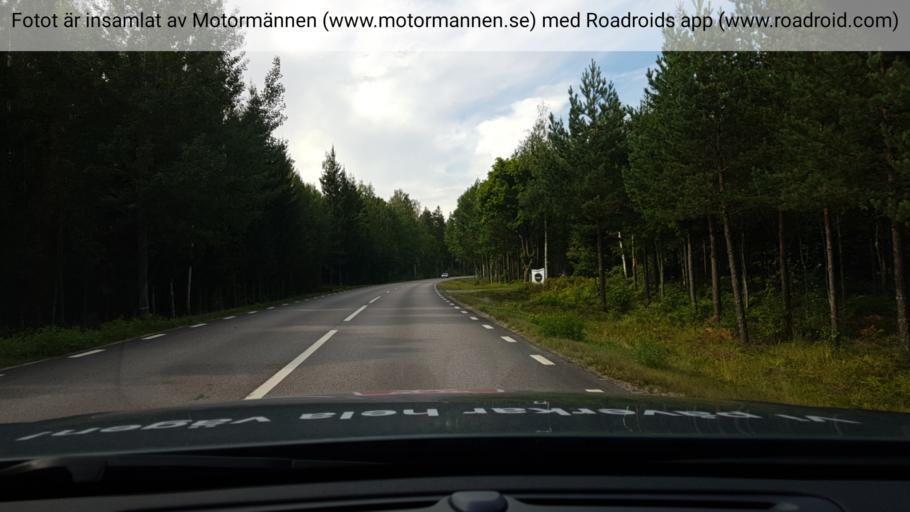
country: SE
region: Gaevleborg
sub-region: Gavle Kommun
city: Hedesunda
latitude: 60.2950
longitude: 16.9090
